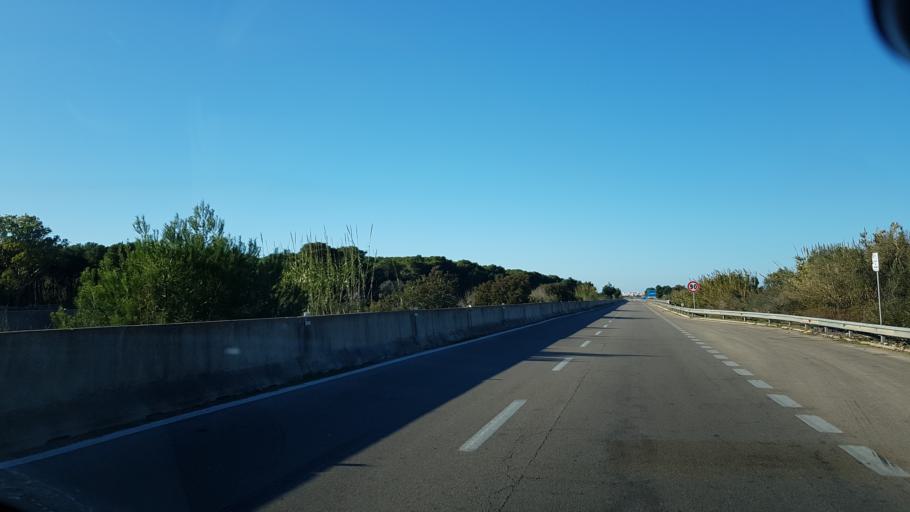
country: IT
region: Apulia
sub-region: Provincia di Lecce
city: Alezio
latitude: 40.0247
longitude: 18.0377
